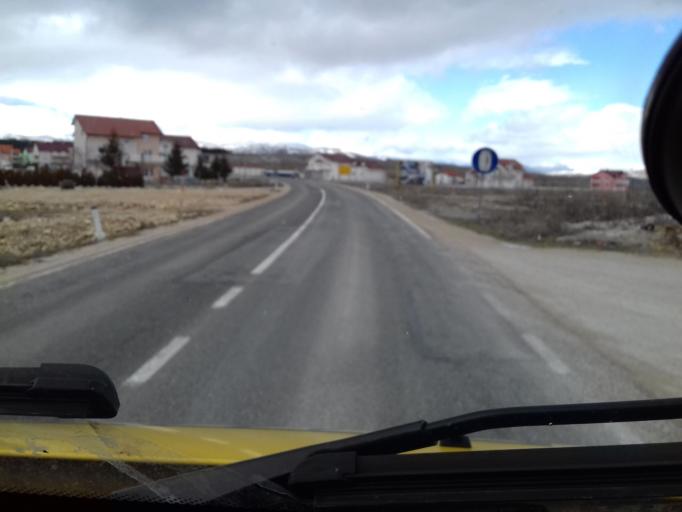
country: BA
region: Federation of Bosnia and Herzegovina
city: Tomislavgrad
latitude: 43.7163
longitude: 17.2386
